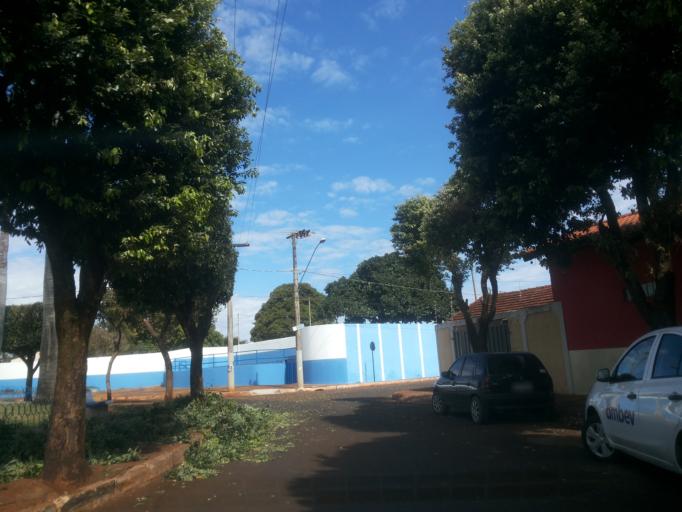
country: BR
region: Minas Gerais
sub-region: Centralina
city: Centralina
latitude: -18.5865
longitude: -49.2014
